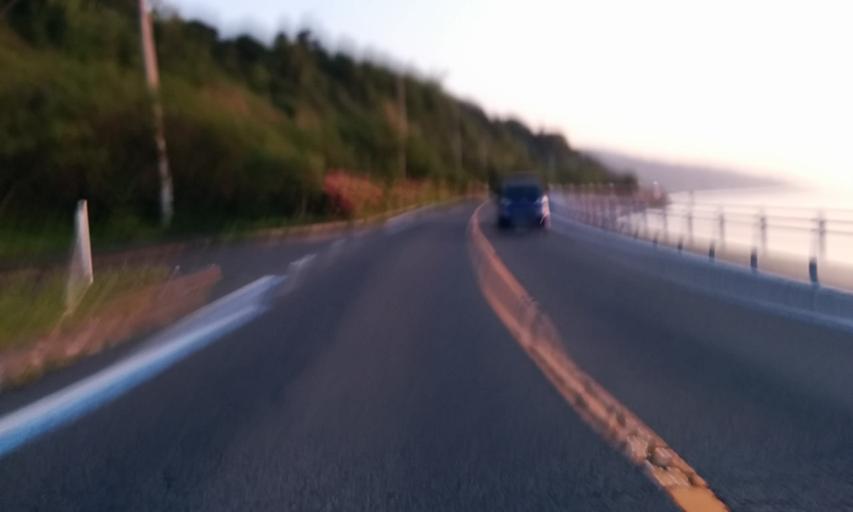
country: JP
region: Ehime
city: Iyo
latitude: 33.6666
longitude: 132.6070
